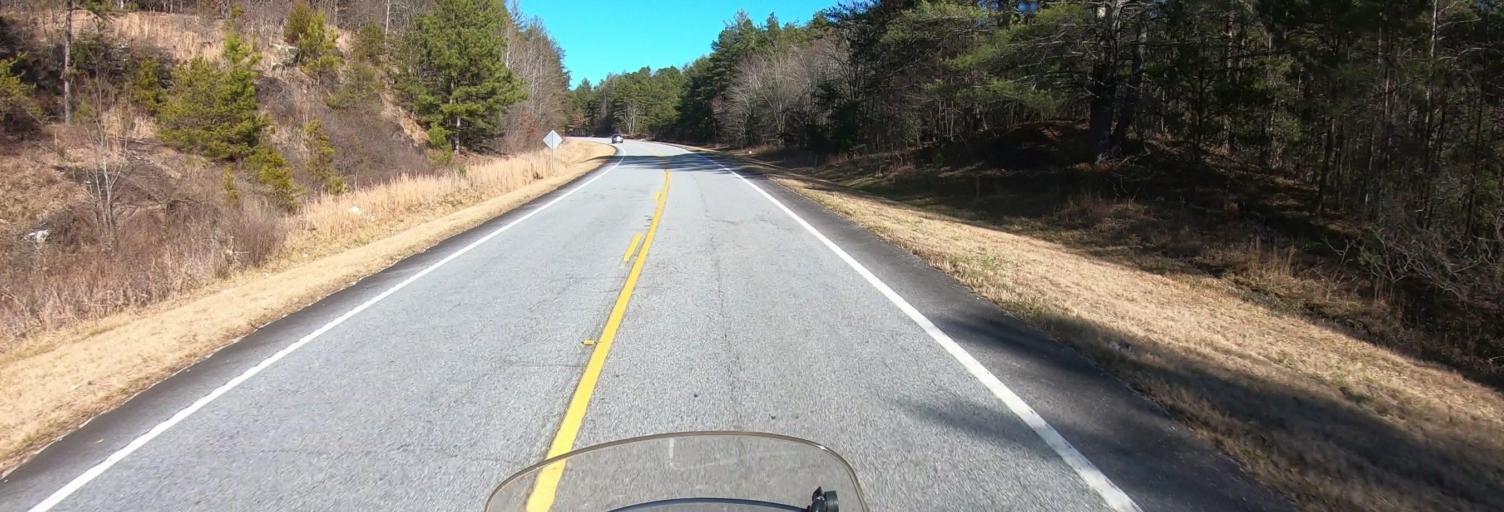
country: US
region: South Carolina
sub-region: Pickens County
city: Pickens
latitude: 34.9480
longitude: -82.8561
